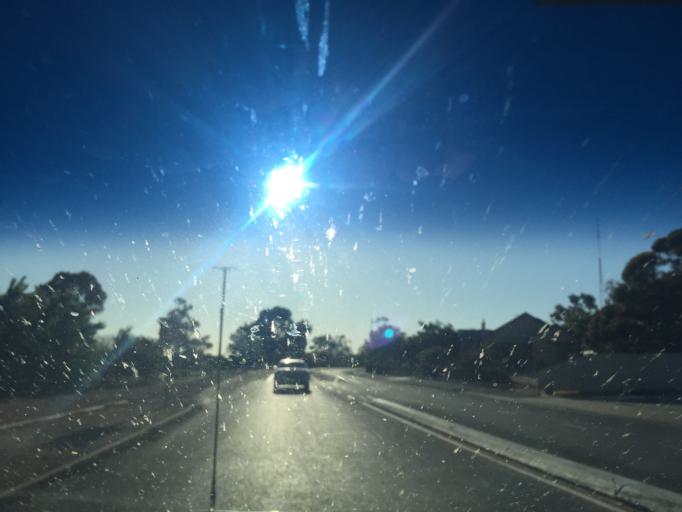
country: AU
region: South Australia
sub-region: Berri and Barmera
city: Berri
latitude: -34.2835
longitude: 140.5961
